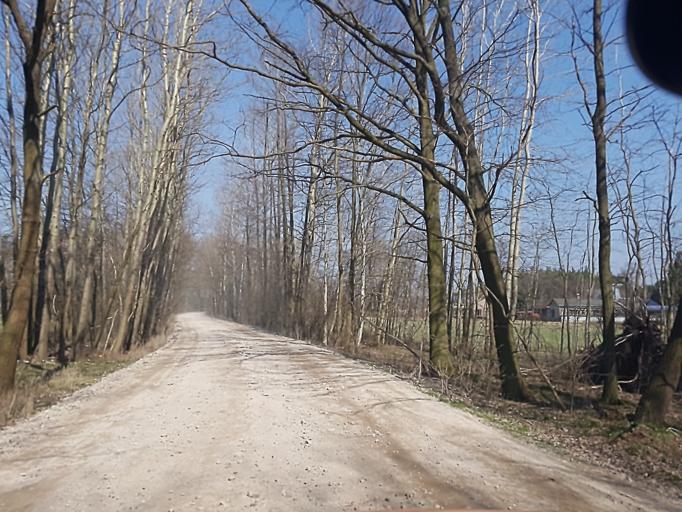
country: DE
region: Brandenburg
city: Forst
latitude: 51.6732
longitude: 14.5730
